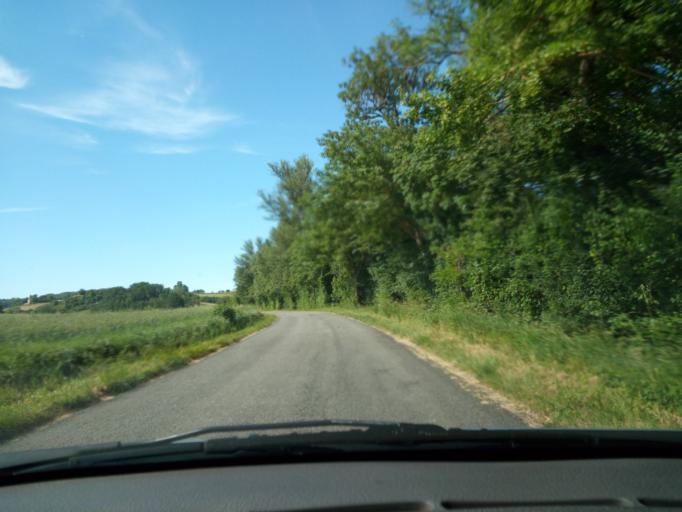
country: FR
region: Midi-Pyrenees
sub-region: Departement du Tarn-et-Garonne
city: Molieres
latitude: 44.2259
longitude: 1.3296
